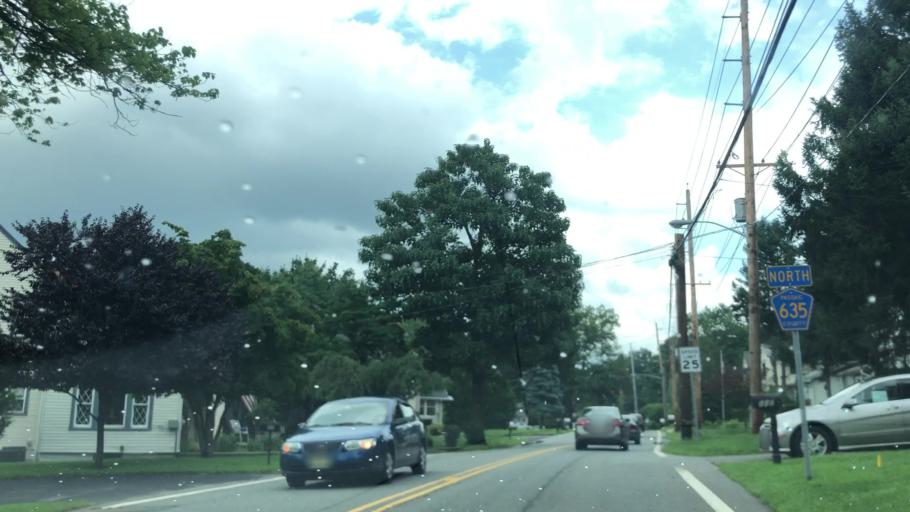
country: US
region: New Jersey
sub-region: Passaic County
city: Little Falls
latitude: 40.8797
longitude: -74.2134
